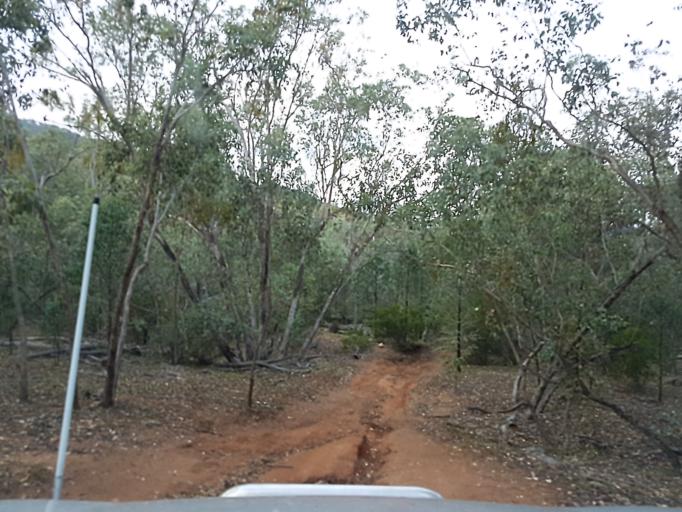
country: AU
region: New South Wales
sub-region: Snowy River
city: Jindabyne
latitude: -36.9481
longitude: 148.3803
